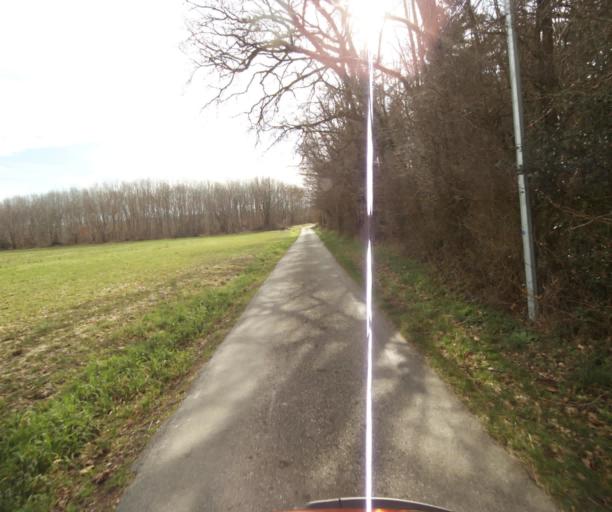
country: FR
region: Midi-Pyrenees
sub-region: Departement de l'Ariege
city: La Tour-du-Crieu
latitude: 43.0891
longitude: 1.7433
